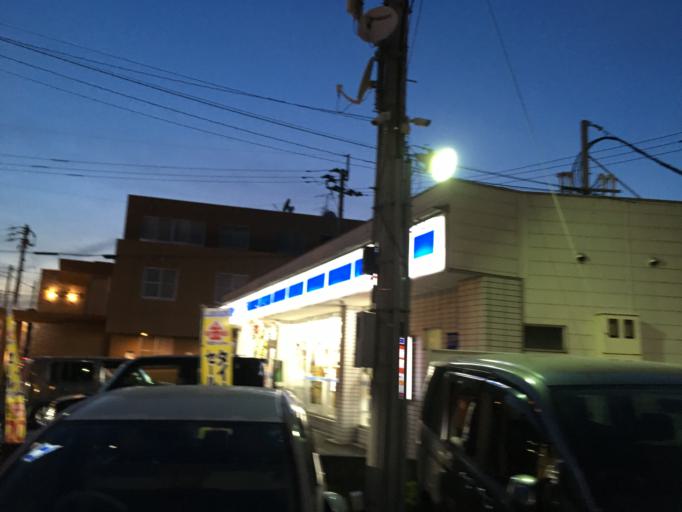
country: JP
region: Kagoshima
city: Kagoshima-shi
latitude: 31.5732
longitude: 130.5558
